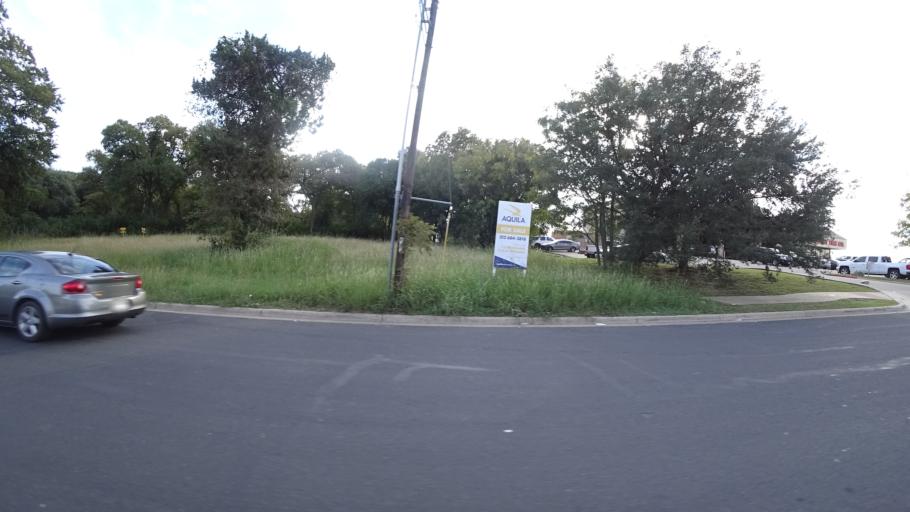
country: US
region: Texas
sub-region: Travis County
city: Onion Creek
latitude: 30.1933
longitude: -97.7664
